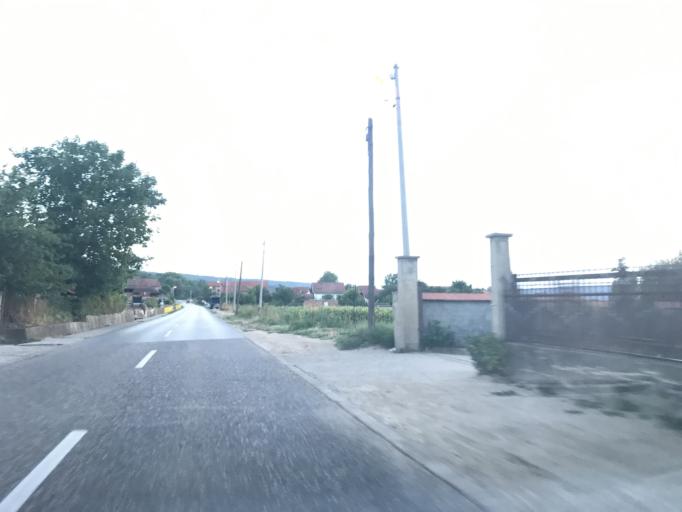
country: RS
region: Central Serbia
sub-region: Branicevski Okrug
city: Veliko Gradiste
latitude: 44.7258
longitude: 21.4577
